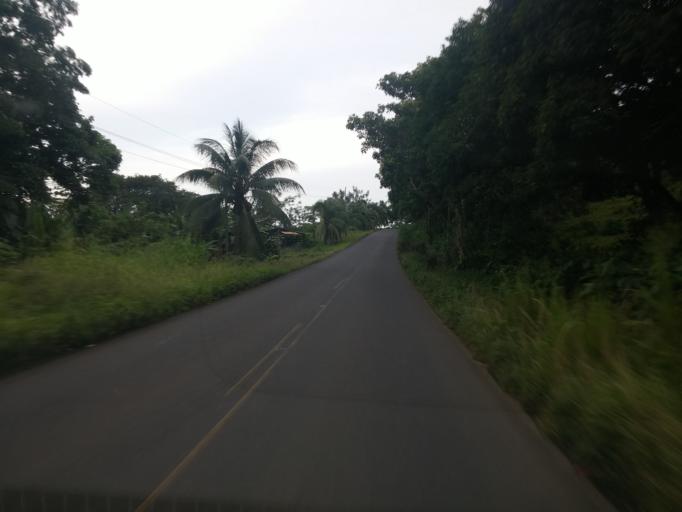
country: CR
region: Alajuela
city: Bijagua
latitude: 10.8099
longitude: -85.0194
